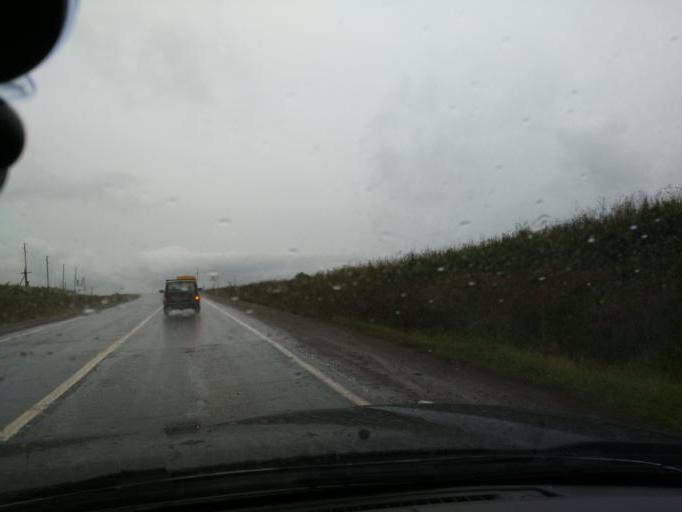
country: RU
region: Perm
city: Yugo-Kamskiy
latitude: 57.6972
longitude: 55.6176
